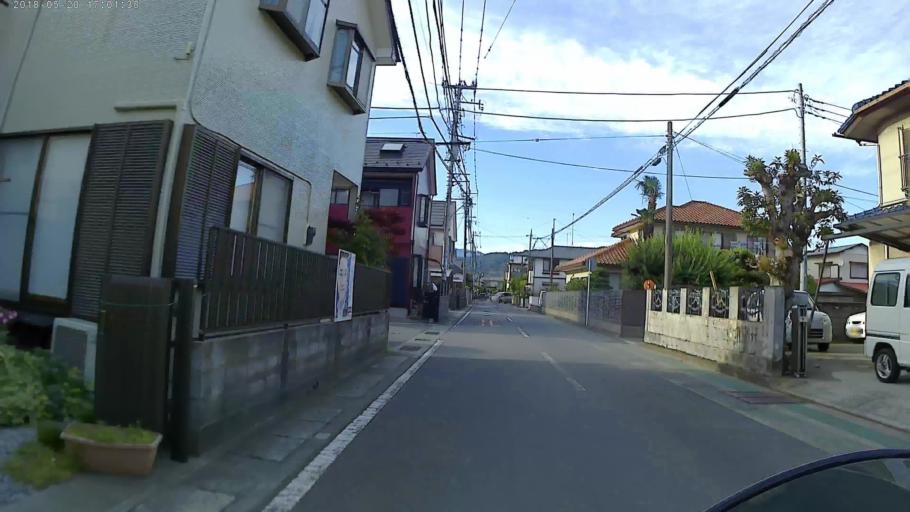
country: JP
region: Kanagawa
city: Odawara
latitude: 35.2865
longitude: 139.1844
